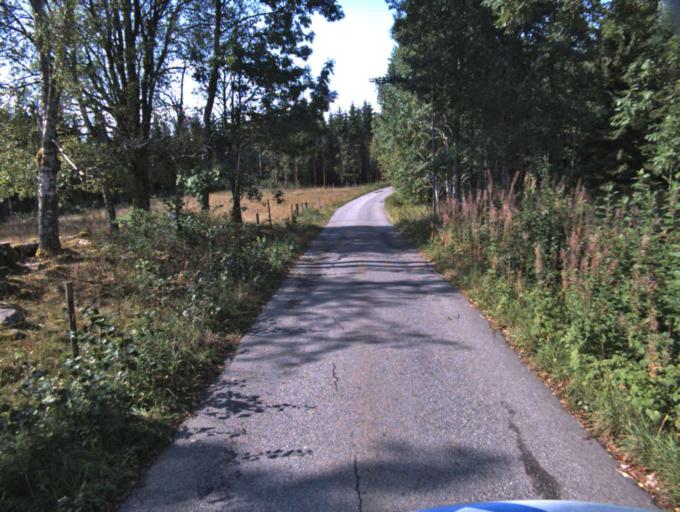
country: SE
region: Vaestra Goetaland
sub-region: Ulricehamns Kommun
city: Ulricehamn
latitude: 57.6744
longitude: 13.4707
